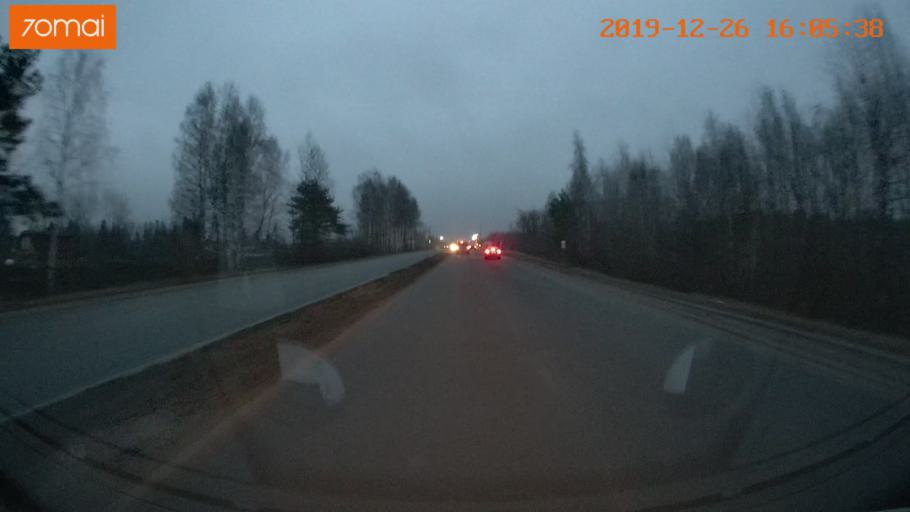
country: RU
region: Jaroslavl
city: Rybinsk
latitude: 58.0060
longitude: 38.9003
